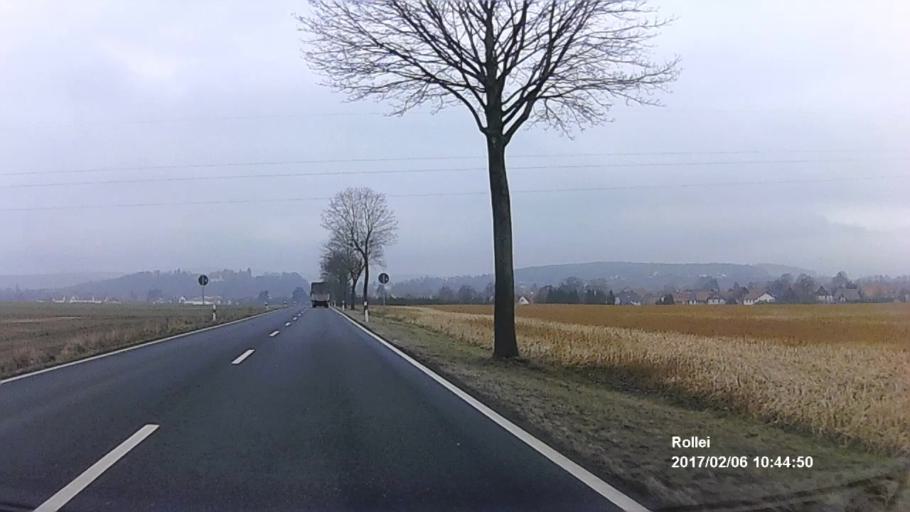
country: DE
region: Lower Saxony
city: Katlenburg-Lindau
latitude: 51.6862
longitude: 10.1207
